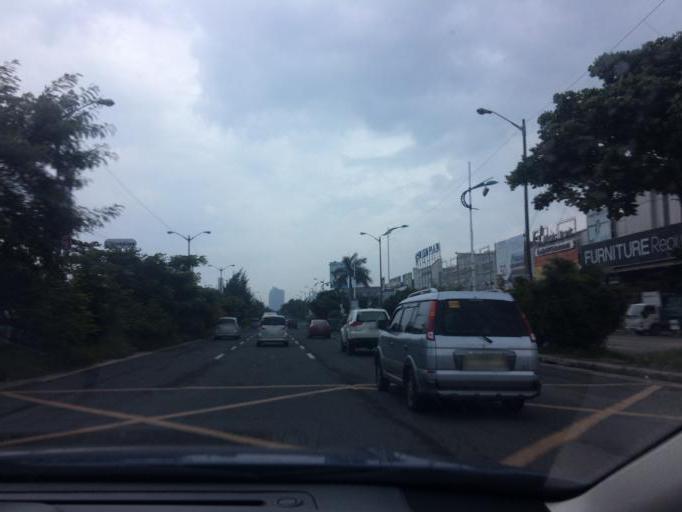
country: PH
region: Metro Manila
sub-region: City of Manila
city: Port Area
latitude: 14.5448
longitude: 120.9877
